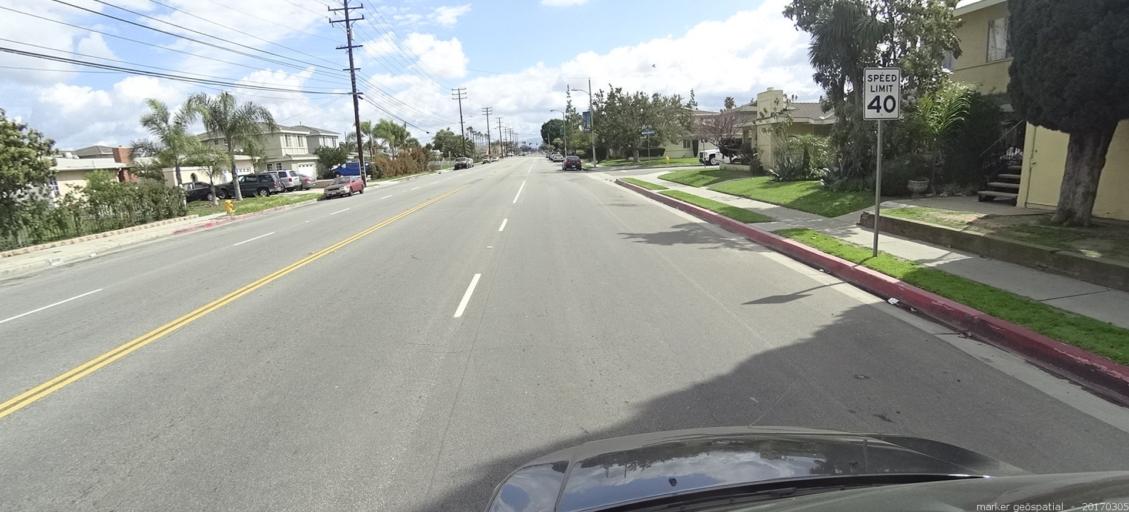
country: US
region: California
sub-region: Orange County
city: Stanton
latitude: 33.8103
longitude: -117.9791
